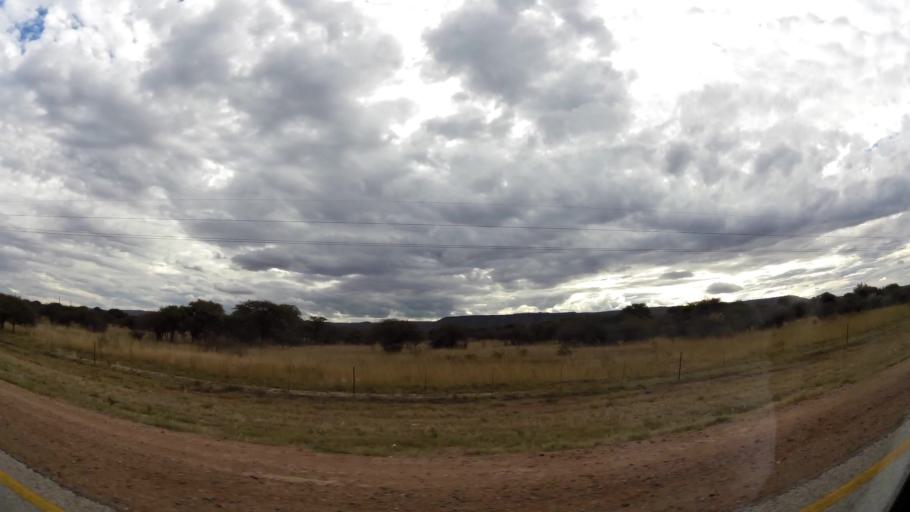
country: ZA
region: Limpopo
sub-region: Waterberg District Municipality
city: Modimolle
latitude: -24.5623
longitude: 28.6827
